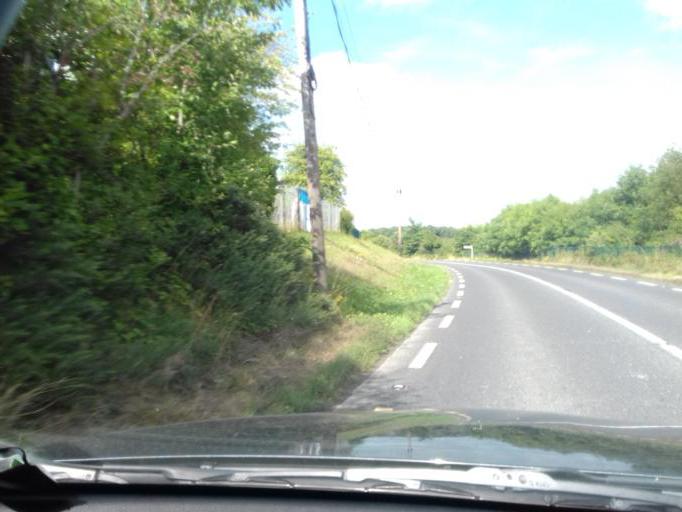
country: IE
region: Leinster
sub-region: Wicklow
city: Valleymount
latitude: 53.1210
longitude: -6.5835
